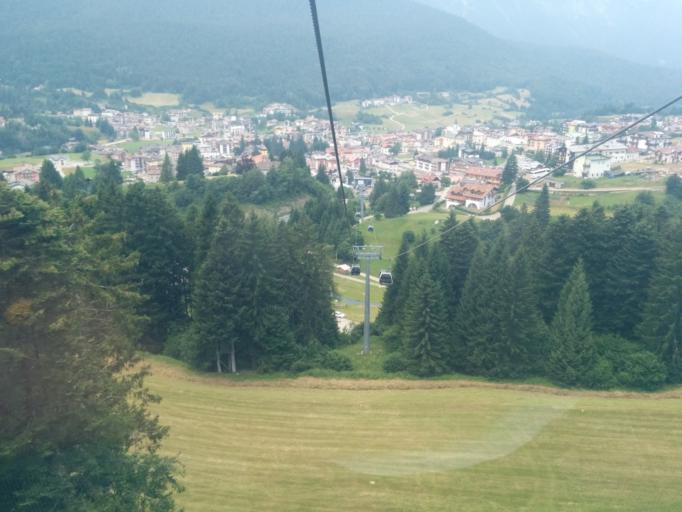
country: IT
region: Trentino-Alto Adige
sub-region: Provincia di Trento
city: Andalo
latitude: 46.1595
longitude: 11.0091
